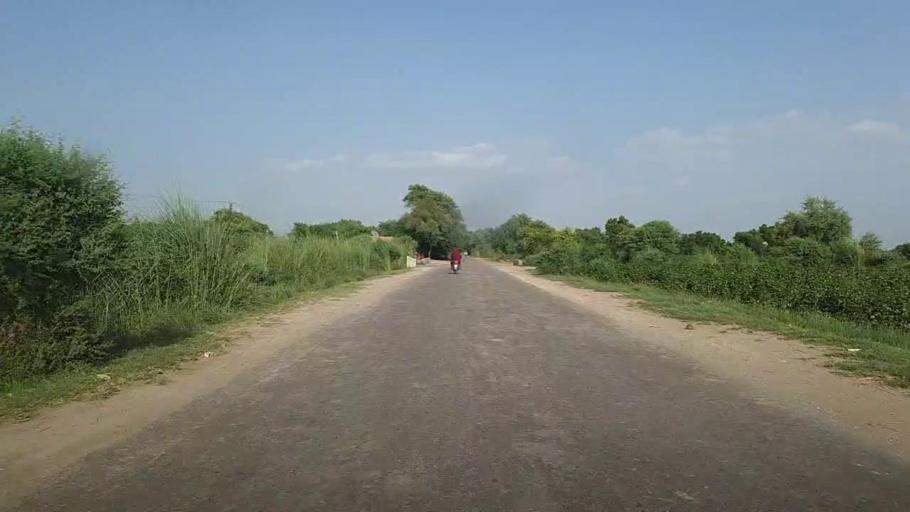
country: PK
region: Sindh
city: Khairpur
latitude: 28.0755
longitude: 69.8107
